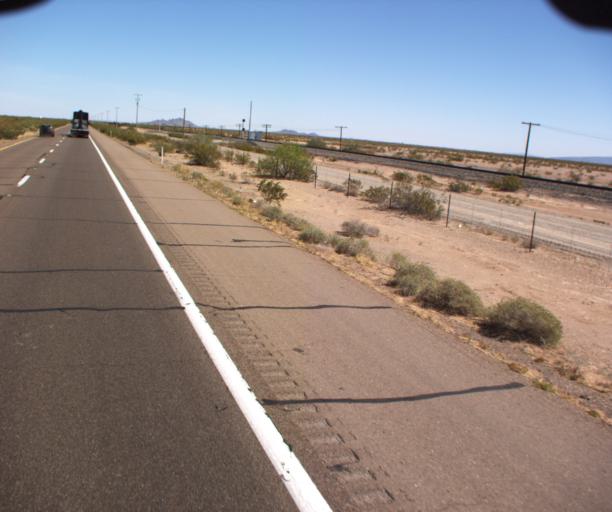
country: US
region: Arizona
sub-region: Yuma County
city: Wellton
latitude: 32.7594
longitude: -113.6381
